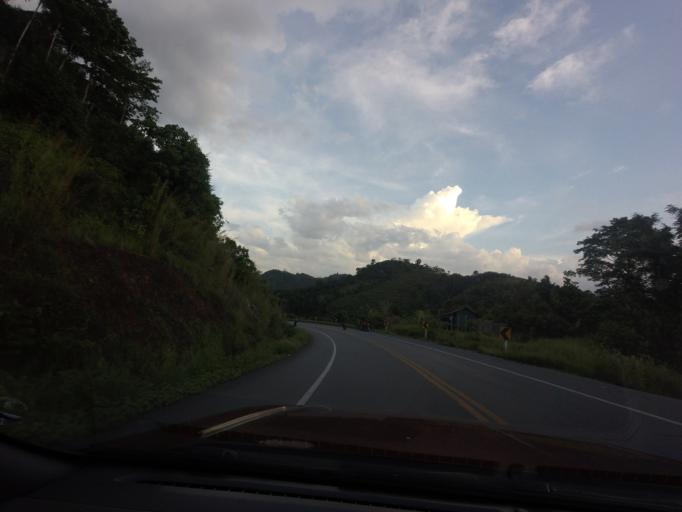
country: TH
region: Yala
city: Than To
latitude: 6.0552
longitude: 101.1932
